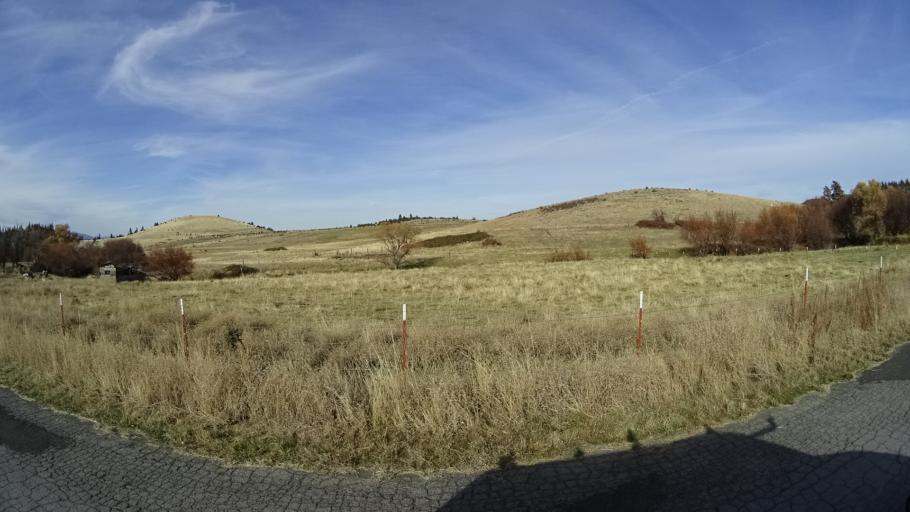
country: US
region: California
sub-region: Siskiyou County
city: Weed
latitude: 41.4650
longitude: -122.3961
